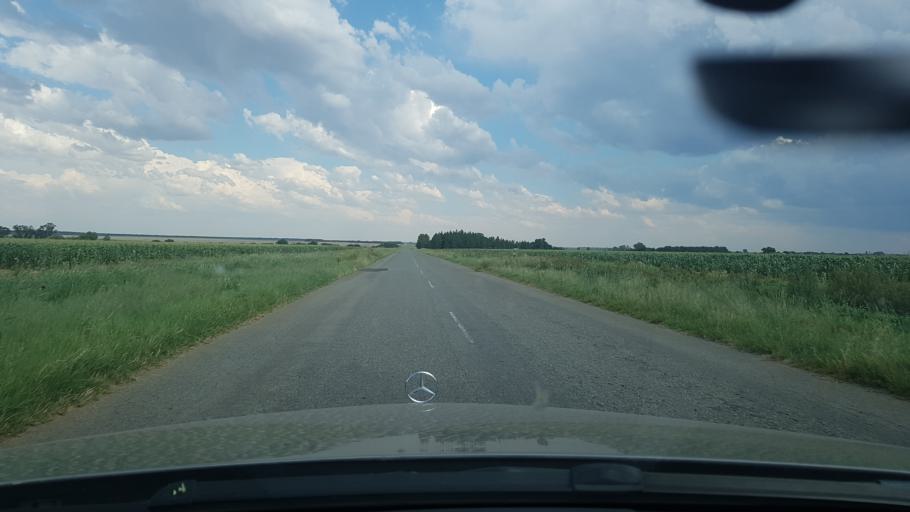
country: ZA
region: North-West
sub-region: Dr Ruth Segomotsi Mompati District Municipality
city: Bloemhof
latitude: -27.8459
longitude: 25.6448
